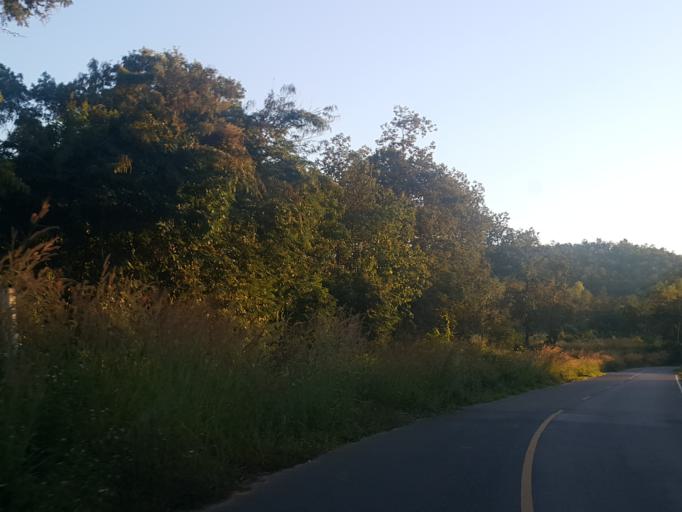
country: TH
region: Chiang Mai
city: San Sai
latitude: 18.8578
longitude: 99.1579
